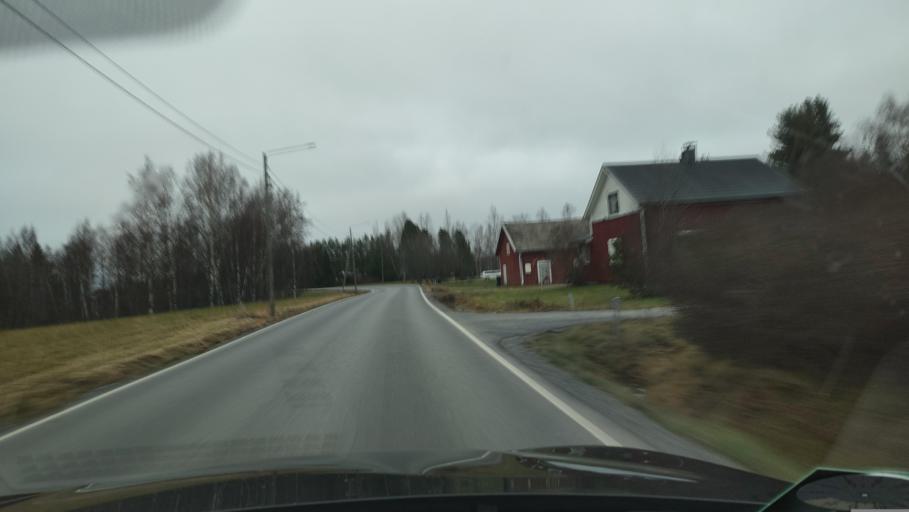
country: FI
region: Southern Ostrobothnia
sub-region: Suupohja
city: Karijoki
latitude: 62.2791
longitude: 21.7095
